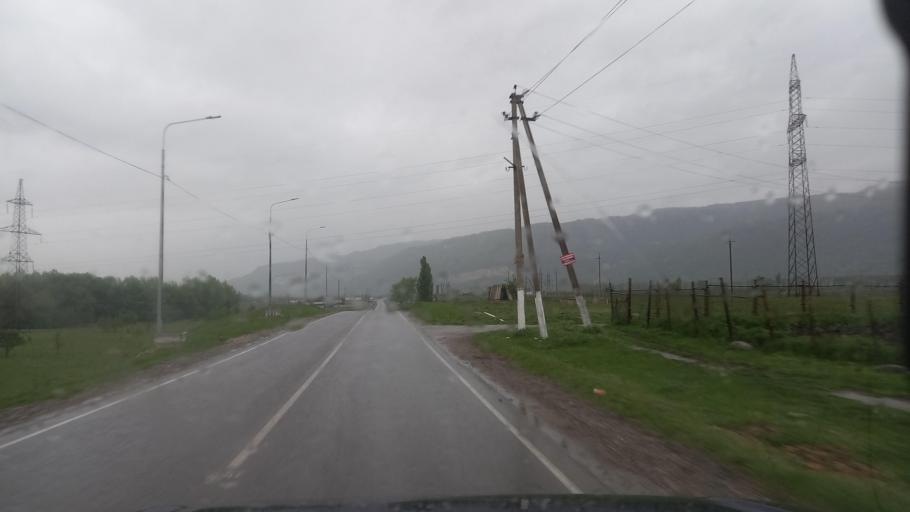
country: RU
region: Kabardino-Balkariya
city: Zhankhoteko
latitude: 43.5883
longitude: 43.2178
